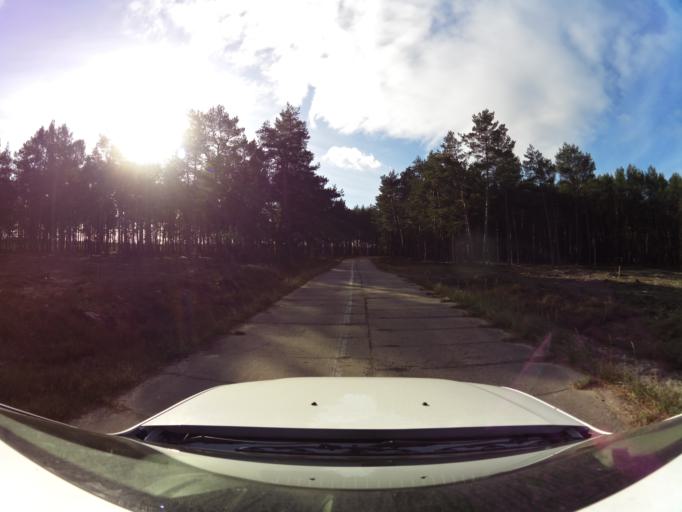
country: PL
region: West Pomeranian Voivodeship
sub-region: Powiat gryficki
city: Cerkwica
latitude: 54.0991
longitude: 15.1402
